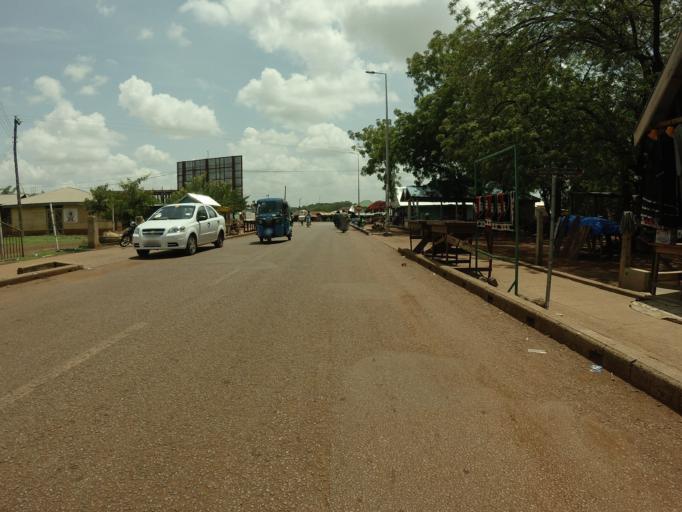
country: GH
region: Northern
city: Tamale
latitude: 9.4022
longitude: -0.8506
